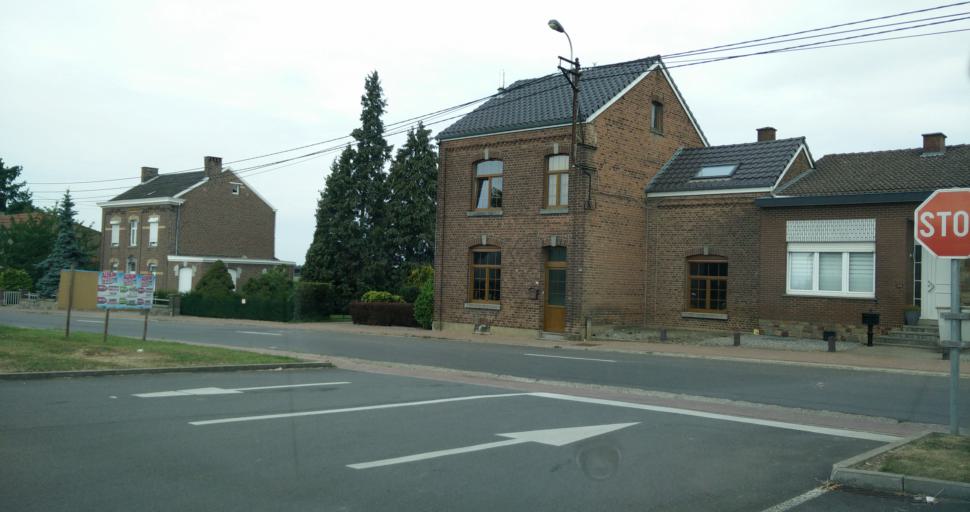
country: BE
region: Wallonia
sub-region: Province de Liege
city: Dalhem
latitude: 50.7356
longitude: 5.7640
